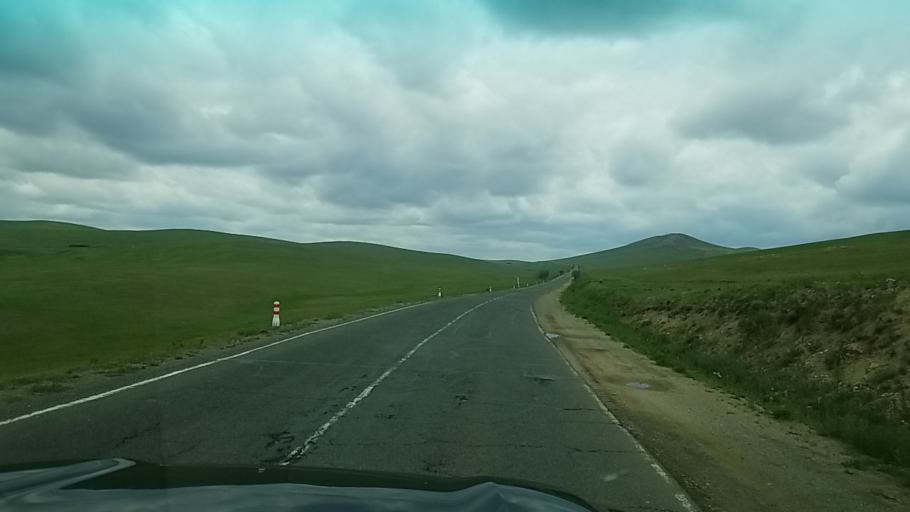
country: MN
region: Darhan Uul
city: Hongor
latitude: 49.1174
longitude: 106.0342
